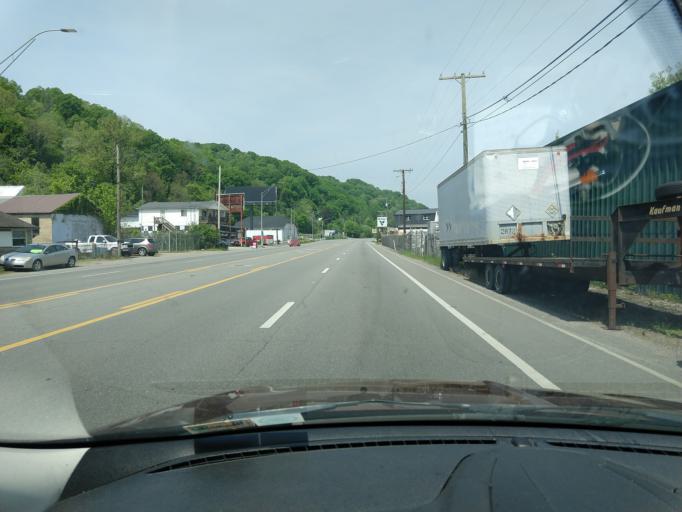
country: US
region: West Virginia
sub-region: Kanawha County
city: Dunbar
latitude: 38.3573
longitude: -81.7542
